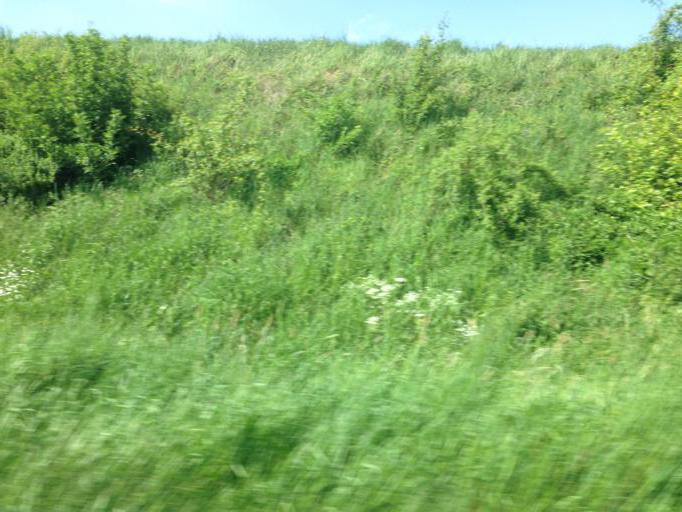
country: DE
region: North Rhine-Westphalia
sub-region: Regierungsbezirk Koln
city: Bad Munstereifel
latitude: 50.5557
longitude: 6.7172
